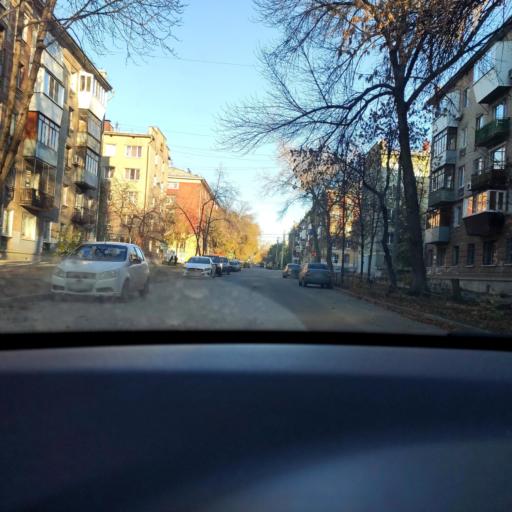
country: RU
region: Samara
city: Samara
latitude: 53.2065
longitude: 50.2419
